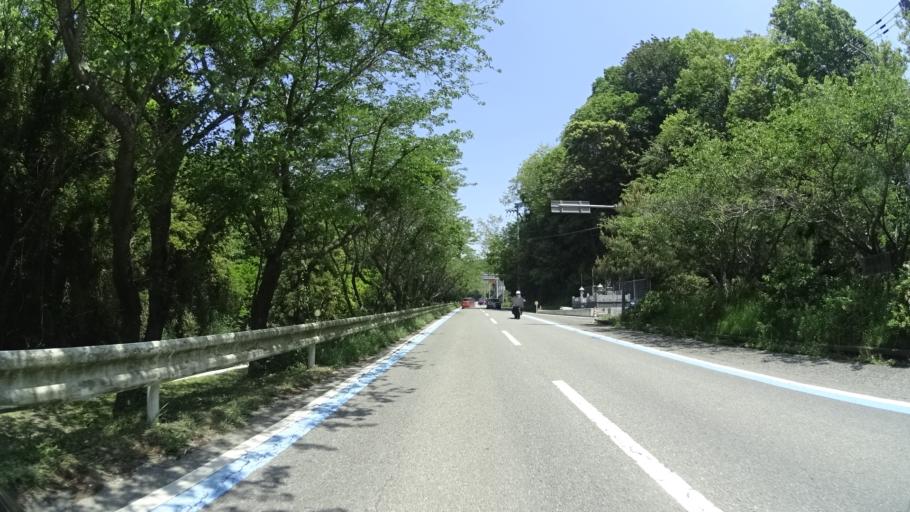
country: JP
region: Ehime
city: Iyo
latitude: 33.7095
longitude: 132.6656
